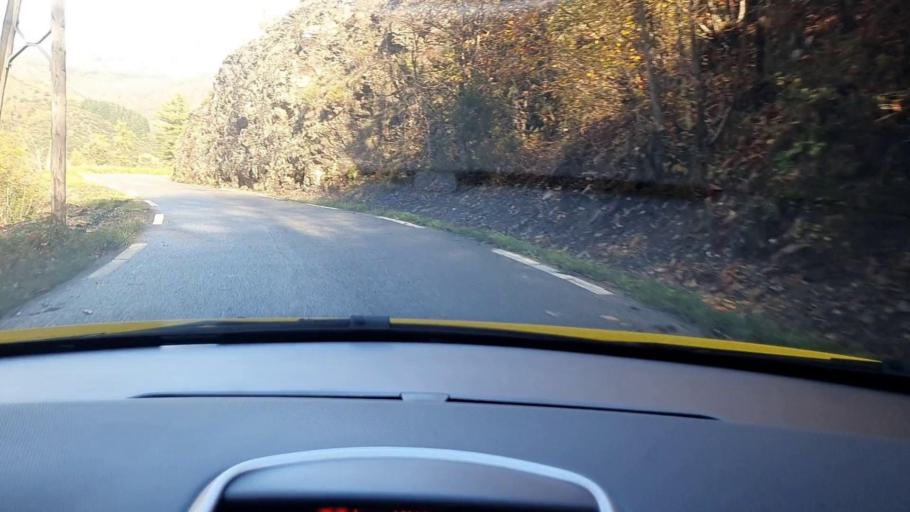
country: FR
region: Languedoc-Roussillon
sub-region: Departement du Gard
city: Valleraugue
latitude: 44.1616
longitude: 3.6418
